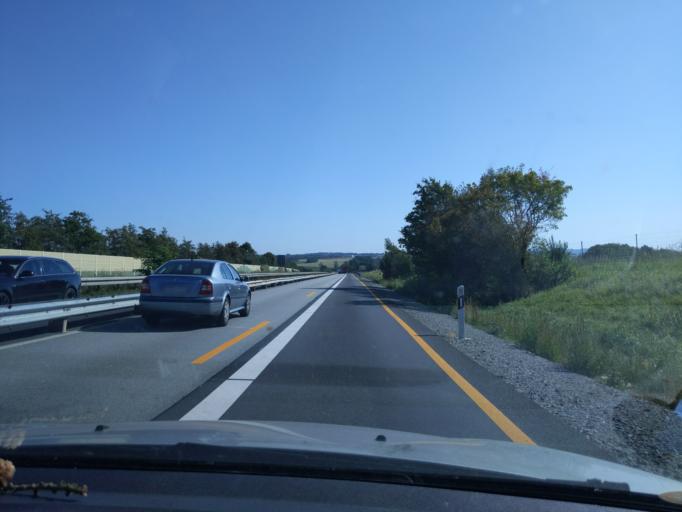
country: DE
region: Saxony
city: Goda
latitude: 51.2018
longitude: 14.2787
